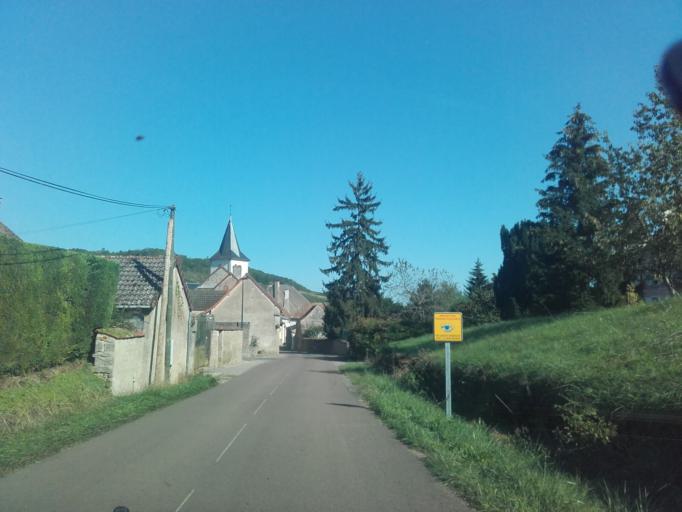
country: FR
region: Bourgogne
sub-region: Departement de la Cote-d'Or
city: Nolay
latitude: 46.9155
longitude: 4.6308
